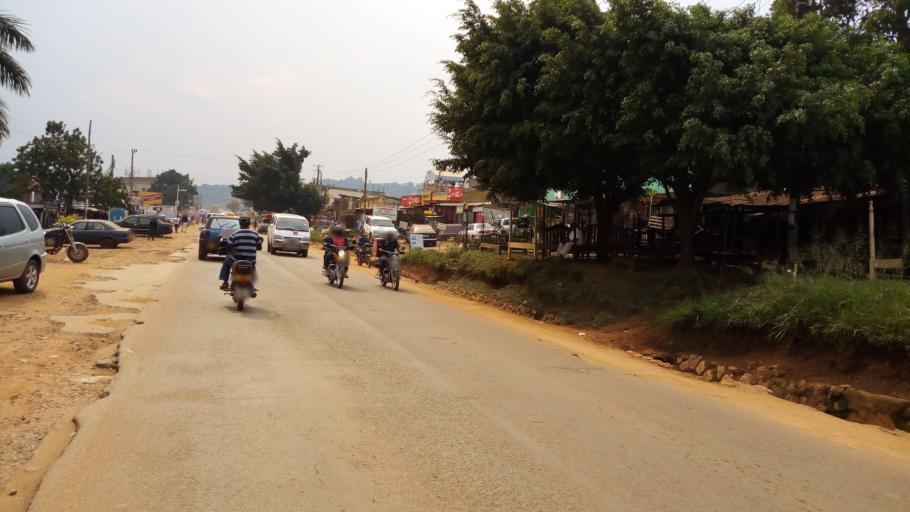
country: UG
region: Central Region
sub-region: Wakiso District
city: Kireka
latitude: 0.3110
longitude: 32.6374
